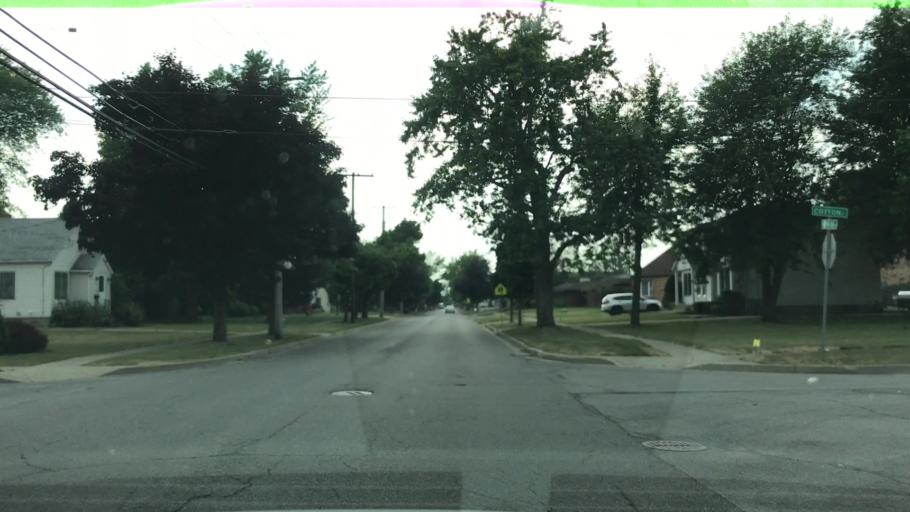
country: US
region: New York
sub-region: Erie County
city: Lancaster
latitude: 42.9079
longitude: -78.6759
